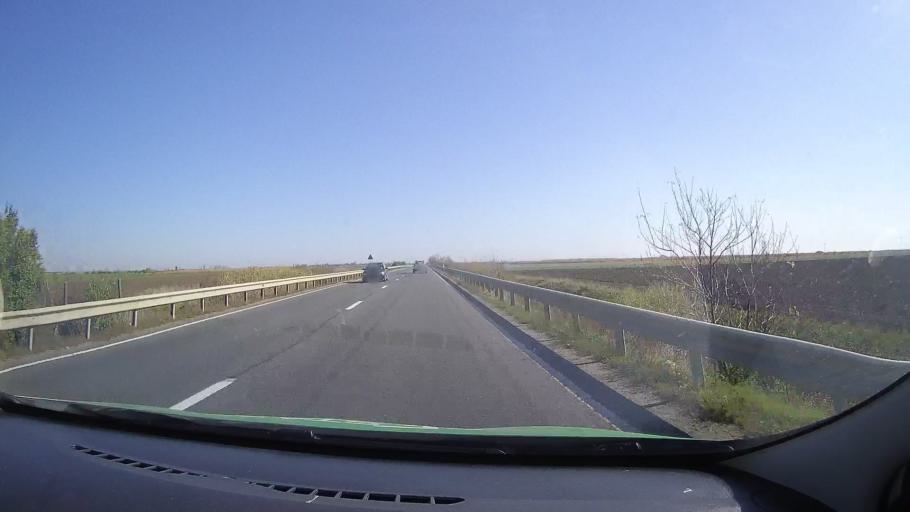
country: RO
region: Satu Mare
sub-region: Comuna Moftinu
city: Domanesti
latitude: 47.6849
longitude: 22.5567
